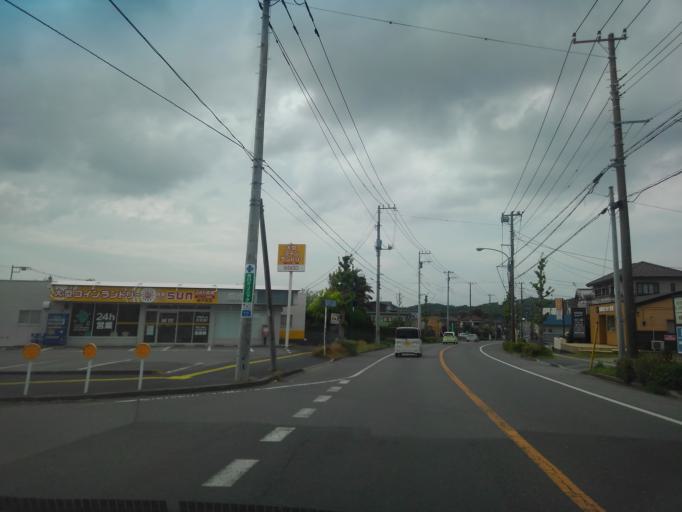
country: JP
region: Chiba
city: Kimitsu
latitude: 35.3296
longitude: 139.9206
